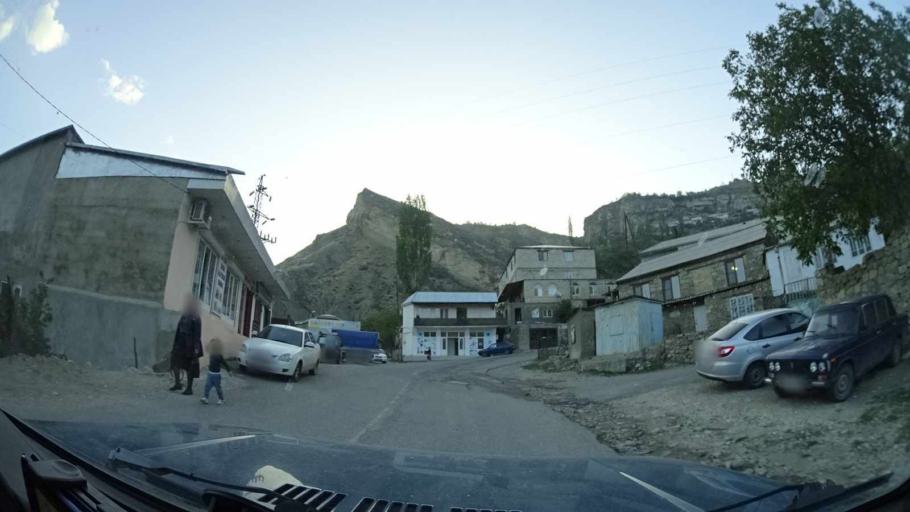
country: RU
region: Dagestan
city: Gunib
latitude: 42.3831
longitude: 46.9627
